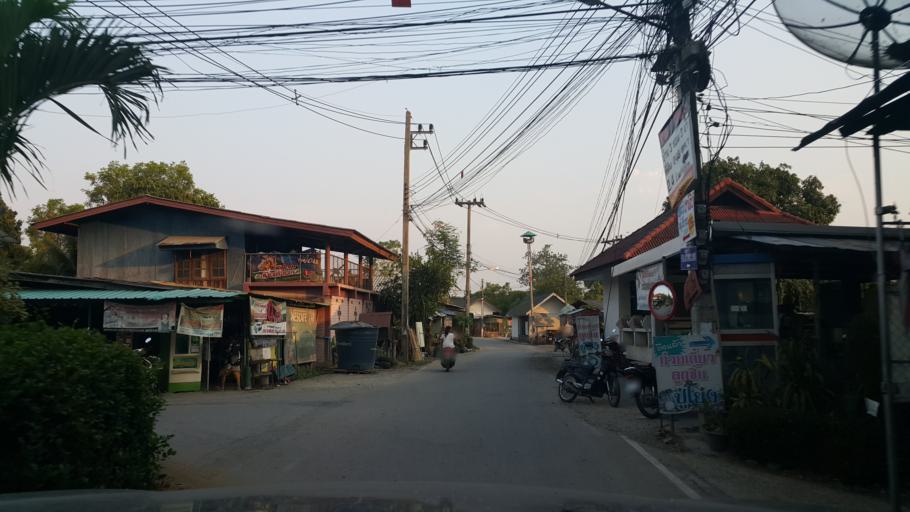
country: TH
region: Chiang Mai
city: Saraphi
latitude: 18.7208
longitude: 99.0228
